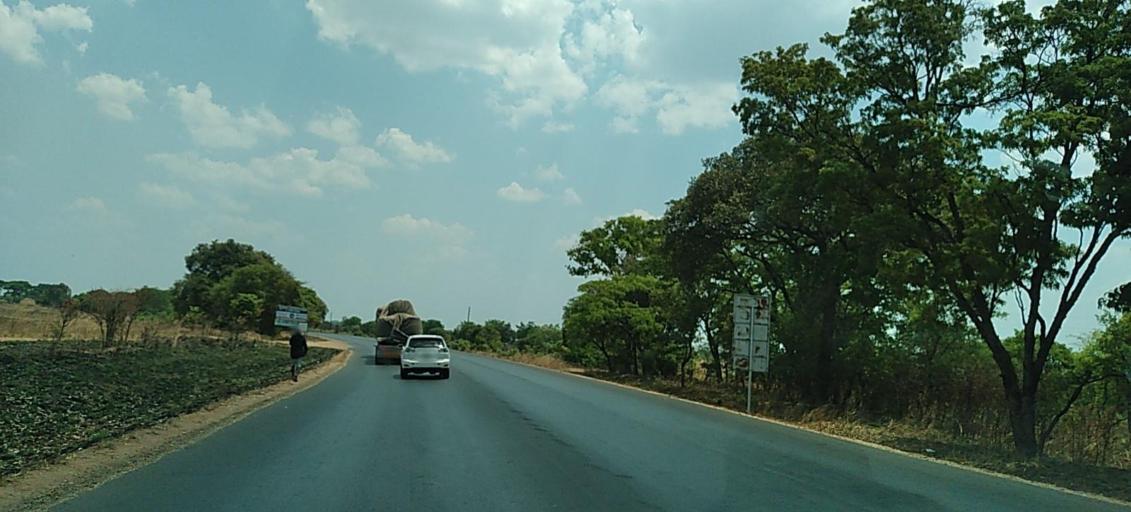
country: ZM
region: Central
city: Kabwe
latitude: -14.2592
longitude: 28.5568
